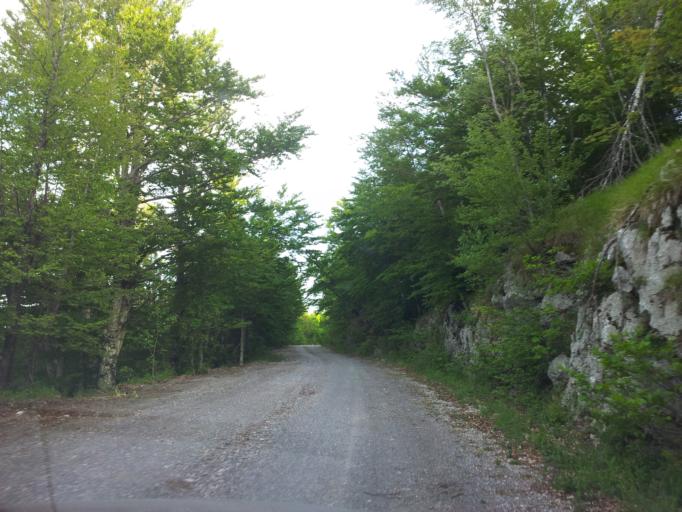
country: HR
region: Zadarska
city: Obrovac
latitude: 44.2974
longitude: 15.6669
